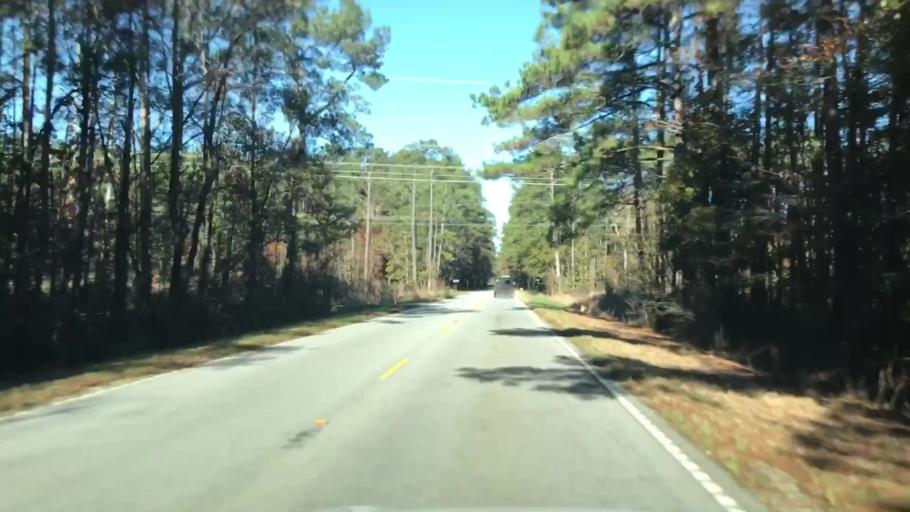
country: US
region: South Carolina
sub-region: Dorchester County
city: Centerville
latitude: 32.9174
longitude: -80.1572
